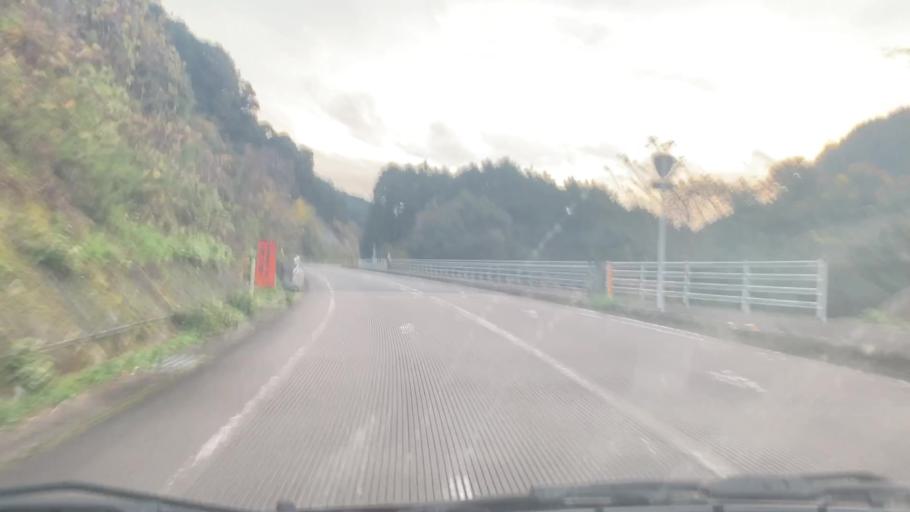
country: JP
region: Saga Prefecture
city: Kashima
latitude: 33.0474
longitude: 130.0716
